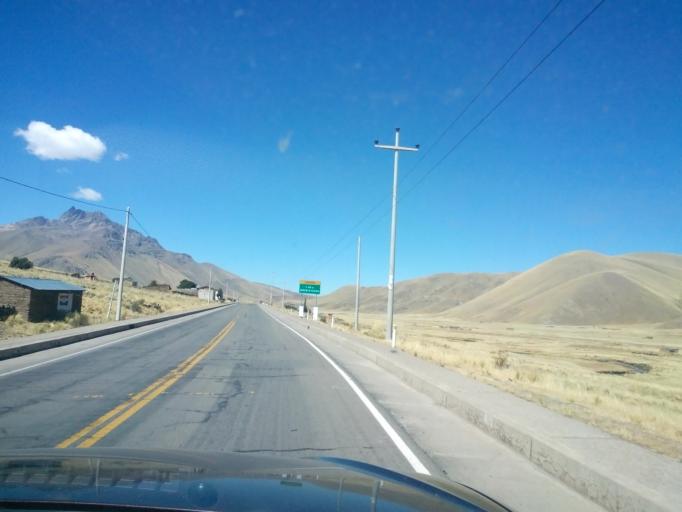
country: PE
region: Puno
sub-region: Provincia de Melgar
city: Santa Rosa
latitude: -14.5134
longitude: -70.9218
